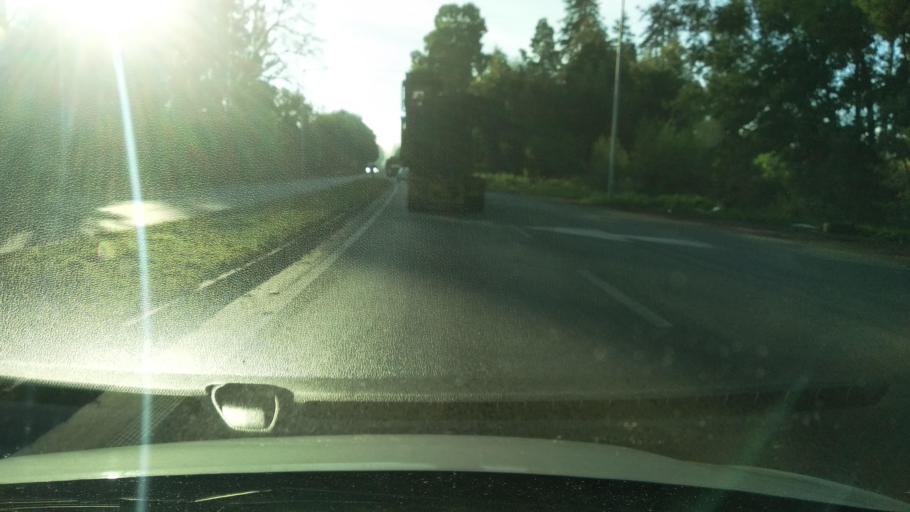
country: CL
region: Los Lagos
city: Las Animas
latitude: -39.7862
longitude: -73.2121
